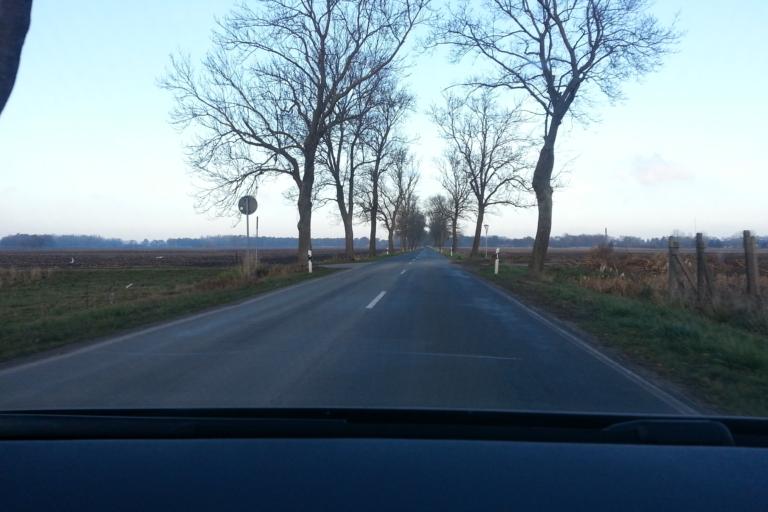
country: DE
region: Mecklenburg-Vorpommern
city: Ferdinandshof
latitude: 53.6465
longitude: 13.8636
